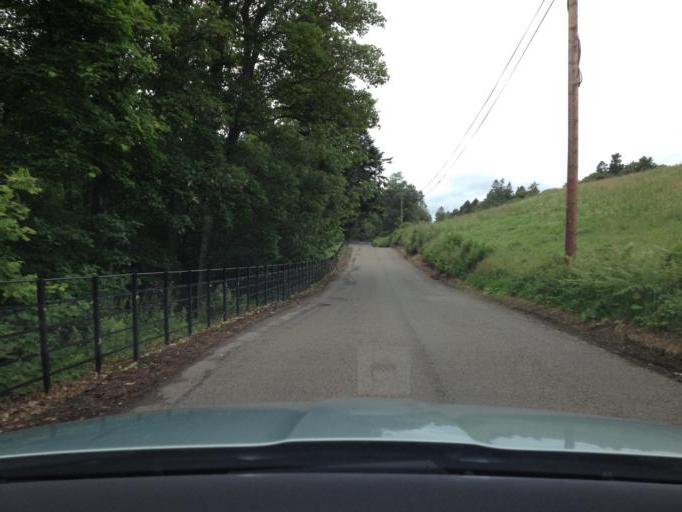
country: GB
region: Scotland
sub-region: Aberdeenshire
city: Aboyne
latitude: 56.8984
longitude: -2.7500
